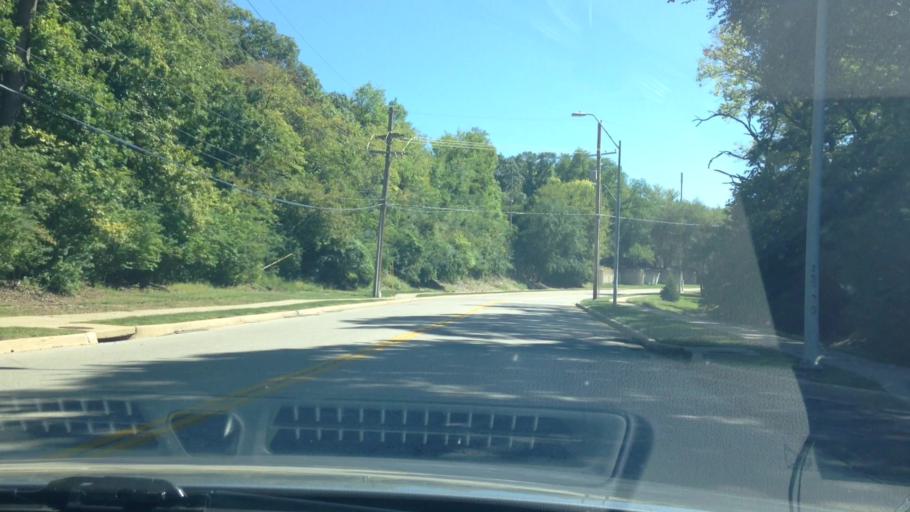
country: US
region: Missouri
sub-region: Jackson County
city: Raytown
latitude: 39.0116
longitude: -94.5055
